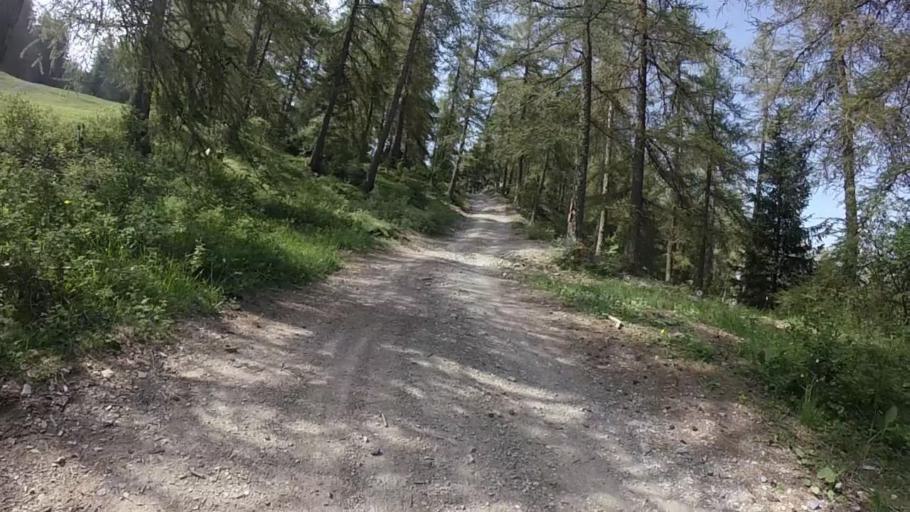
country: FR
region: Provence-Alpes-Cote d'Azur
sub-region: Departement des Alpes-de-Haute-Provence
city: Seyne-les-Alpes
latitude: 44.4039
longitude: 6.3621
